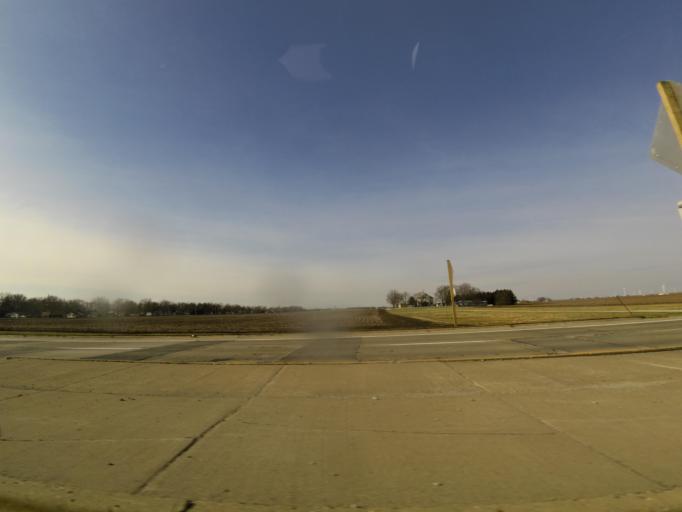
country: US
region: Illinois
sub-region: Macon County
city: Forsyth
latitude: 39.9369
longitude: -88.9556
